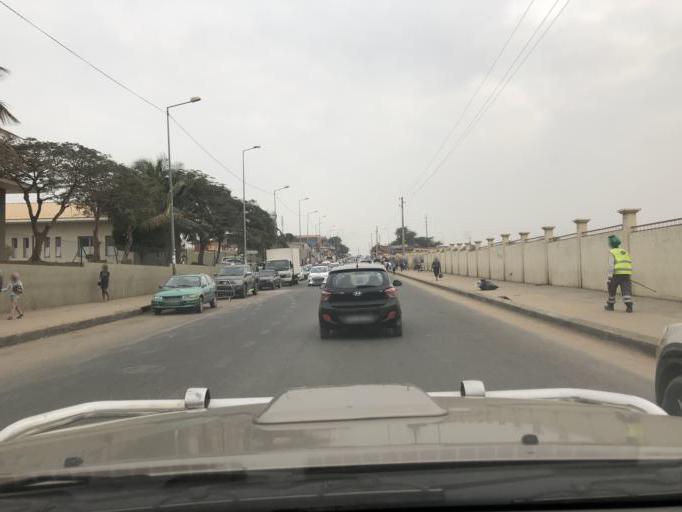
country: AO
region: Luanda
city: Luanda
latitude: -8.9019
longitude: 13.2152
